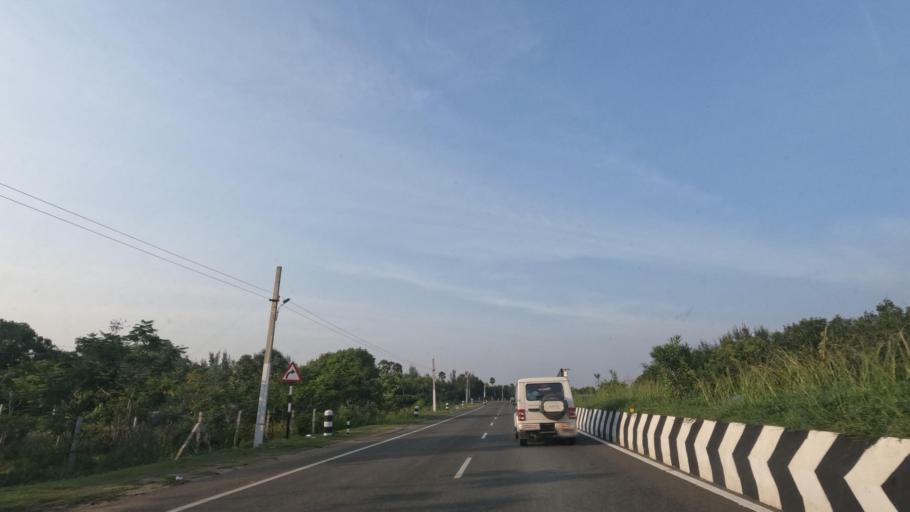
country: IN
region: Tamil Nadu
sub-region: Kancheepuram
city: Mamallapuram
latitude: 12.6661
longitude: 80.2097
